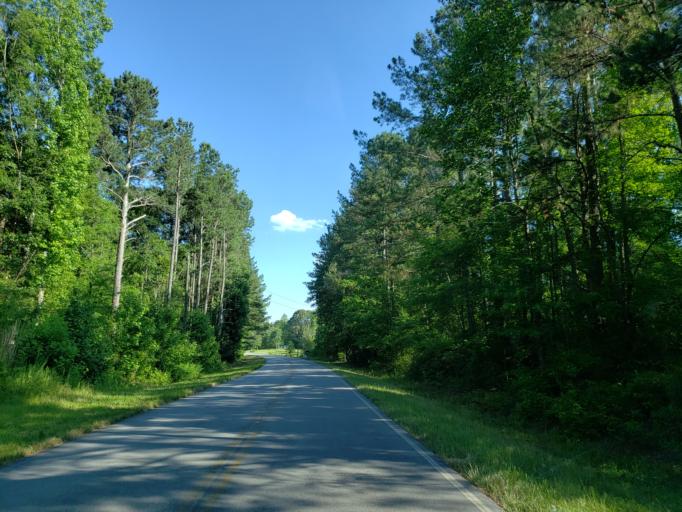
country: US
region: Georgia
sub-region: Haralson County
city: Bremen
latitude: 33.6813
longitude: -85.0875
